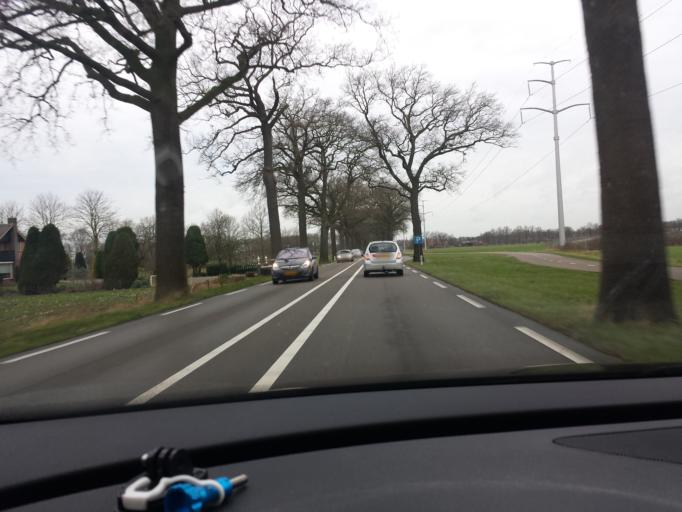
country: NL
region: Gelderland
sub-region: Oost Gelre
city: Lichtenvoorde
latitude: 52.0231
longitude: 6.6351
